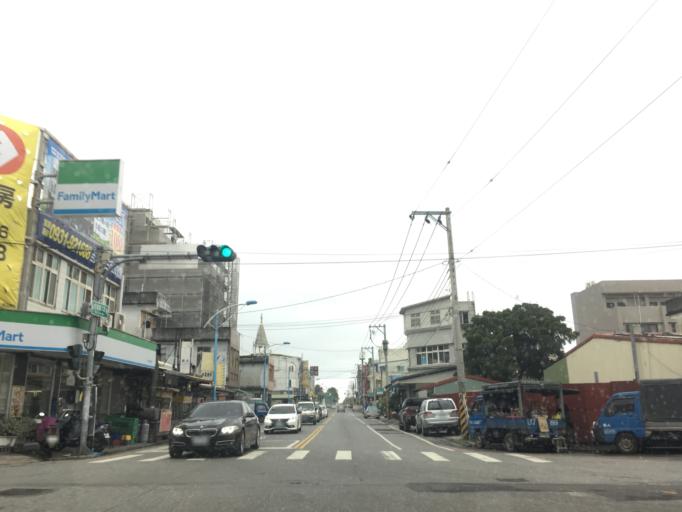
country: TW
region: Taiwan
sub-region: Hualien
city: Hualian
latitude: 23.9796
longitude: 121.5672
